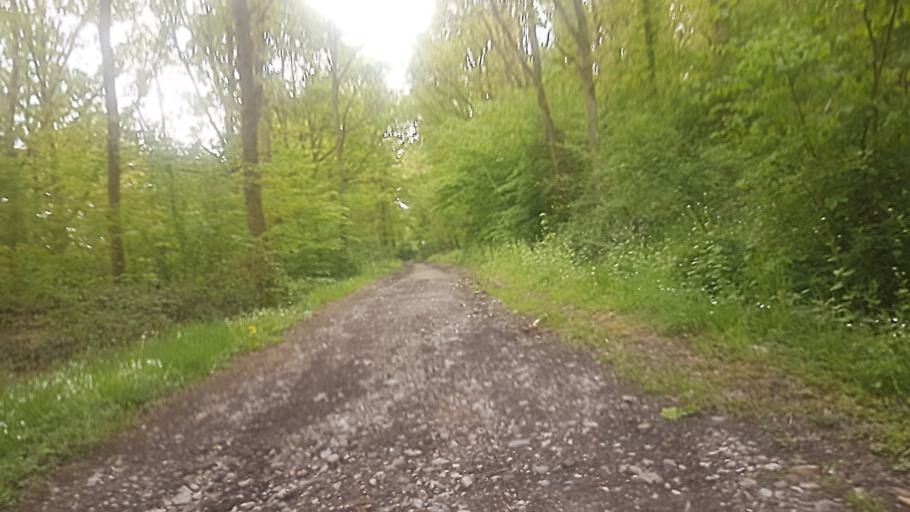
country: BE
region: Wallonia
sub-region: Province de Namur
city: Couvin
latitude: 50.0631
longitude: 4.6043
